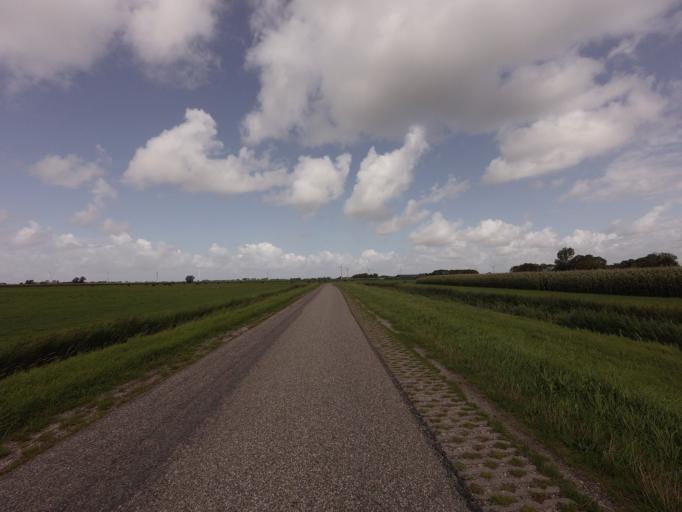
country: NL
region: Friesland
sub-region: Gemeente Franekeradeel
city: Sexbierum
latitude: 53.1687
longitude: 5.4858
